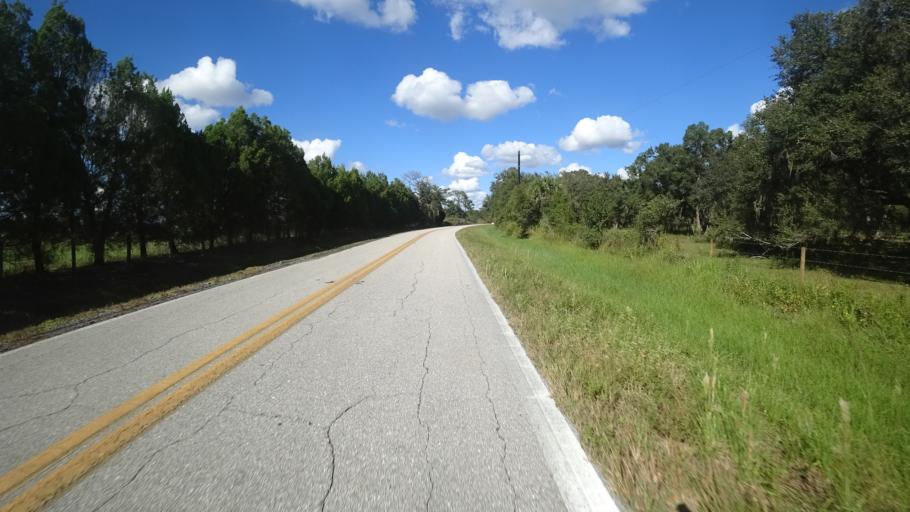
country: US
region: Florida
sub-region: Sarasota County
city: Warm Mineral Springs
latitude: 27.2577
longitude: -82.1218
